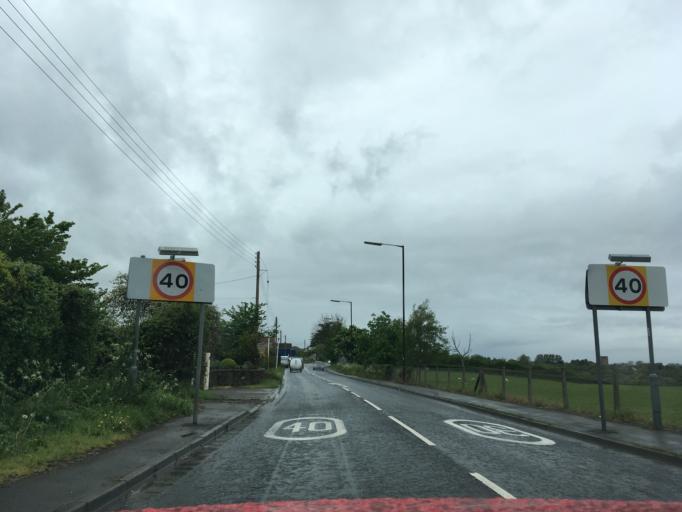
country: GB
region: England
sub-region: North Somerset
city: Banwell
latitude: 51.3297
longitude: -2.8817
